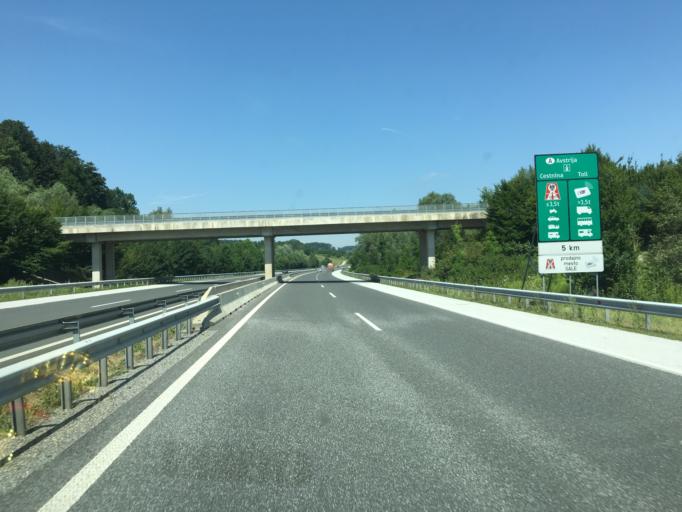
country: SI
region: Kungota
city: Zgornja Kungota
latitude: 46.6428
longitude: 15.6513
